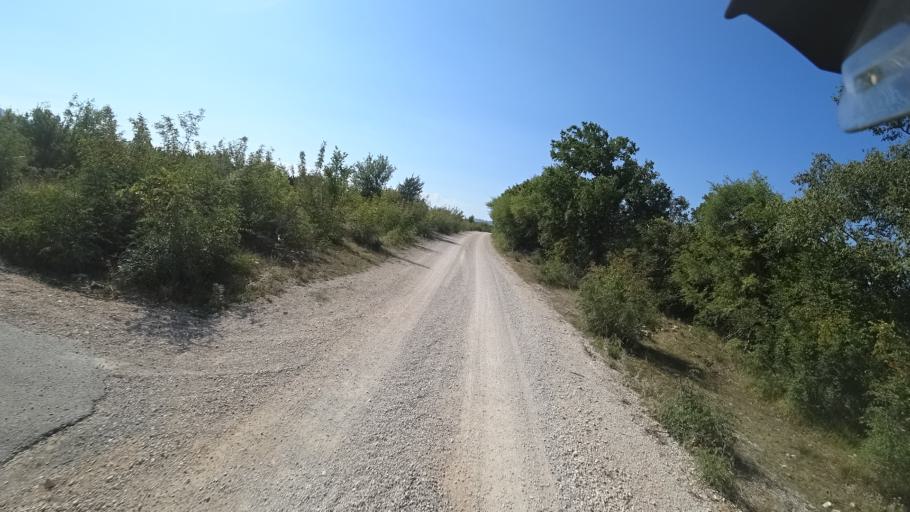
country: HR
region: Sibensko-Kniniska
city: Knin
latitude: 43.9964
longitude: 16.1933
